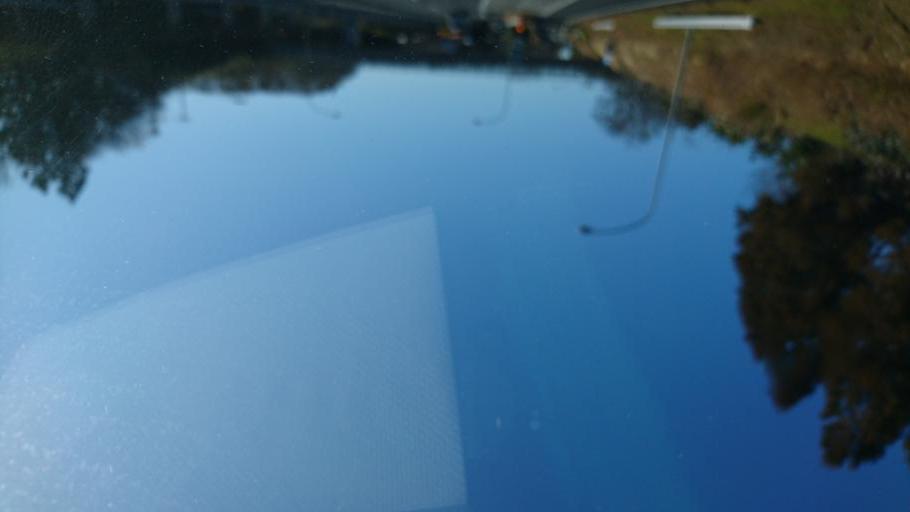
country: JP
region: Chiba
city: Oami
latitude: 35.5699
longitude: 140.2317
